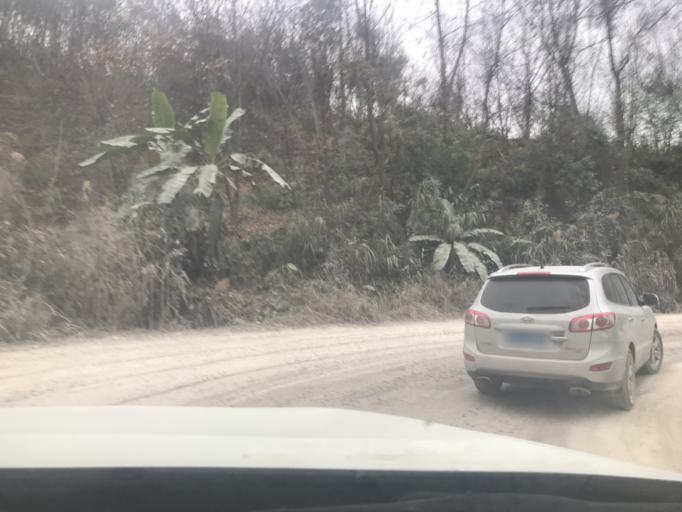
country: CN
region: Guangxi Zhuangzu Zizhiqu
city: Xinzhou
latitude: 25.0056
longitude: 105.8393
